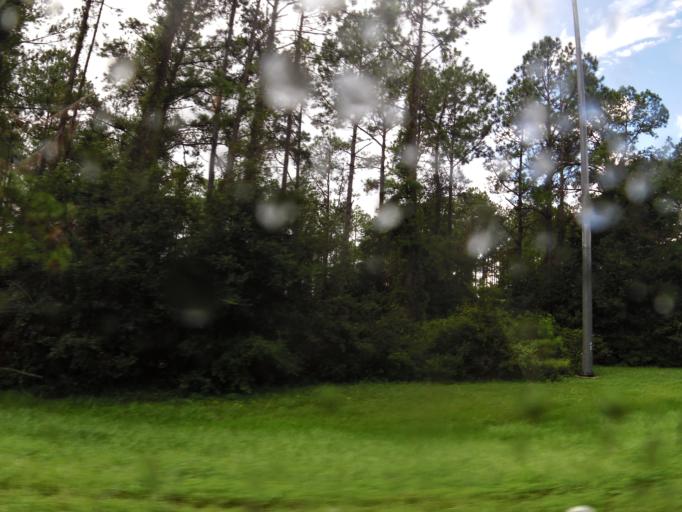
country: US
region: Florida
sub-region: Nassau County
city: Nassau Village-Ratliff
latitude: 30.4122
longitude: -81.7454
